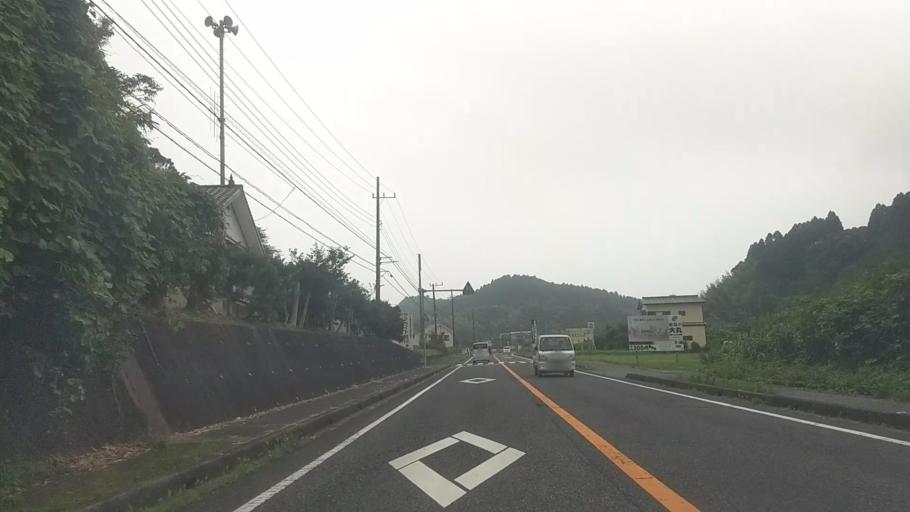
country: JP
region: Chiba
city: Ohara
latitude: 35.2062
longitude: 140.3744
